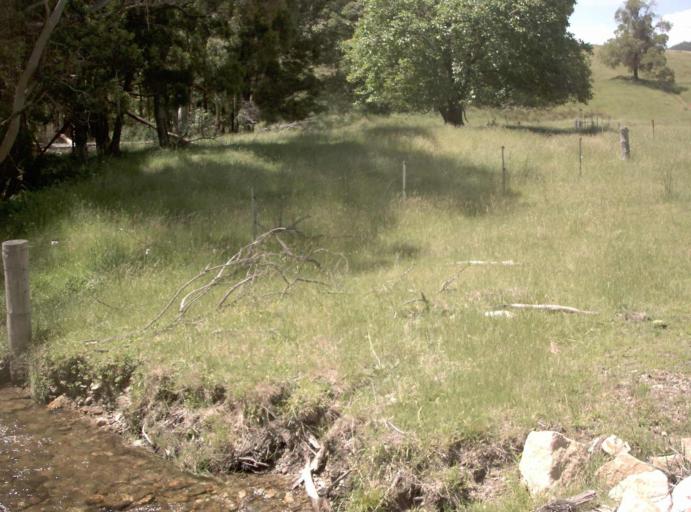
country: AU
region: New South Wales
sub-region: Bombala
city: Bombala
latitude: -37.3590
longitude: 149.0233
